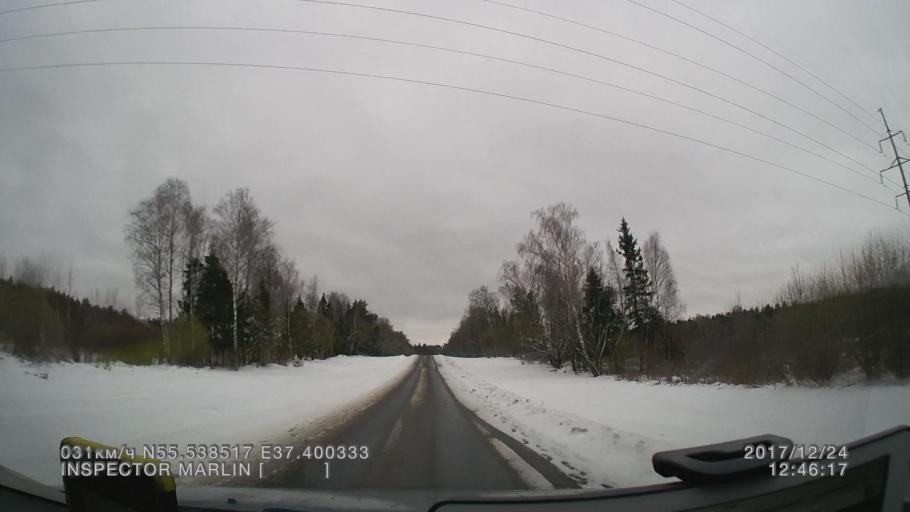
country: RU
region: Moskovskaya
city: Filimonki
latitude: 55.5385
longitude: 37.4004
